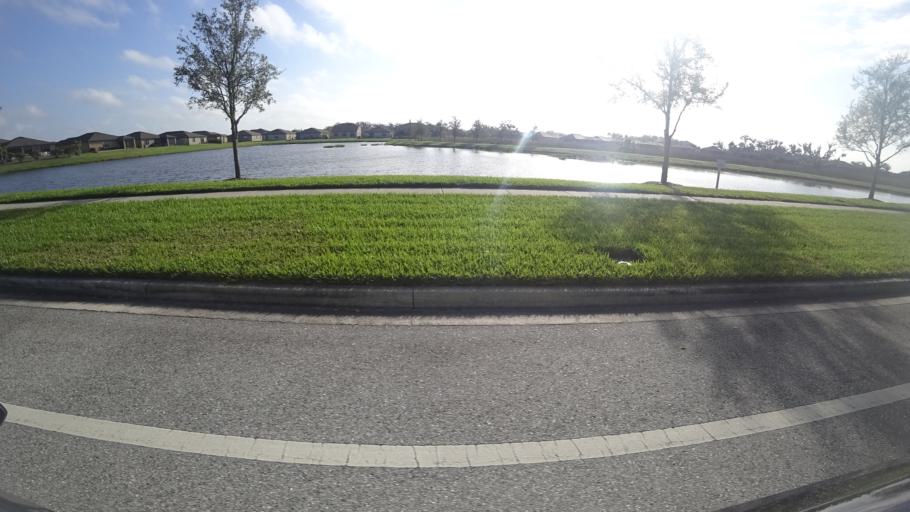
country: US
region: Florida
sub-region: Manatee County
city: Ellenton
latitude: 27.5627
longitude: -82.4581
